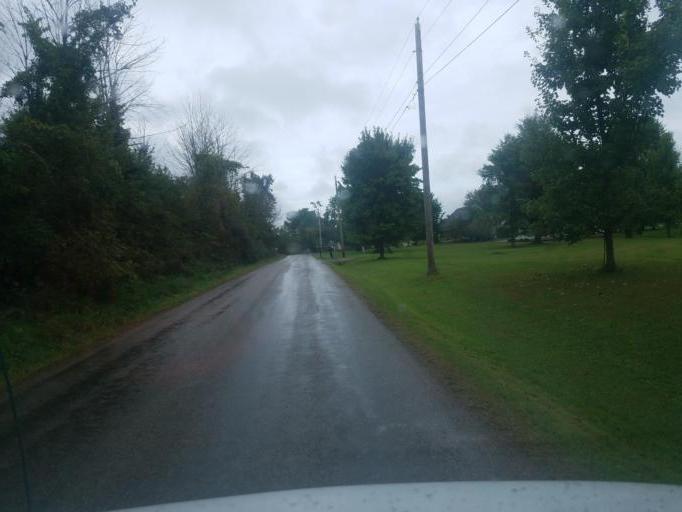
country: US
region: Ohio
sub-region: Wayne County
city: West Salem
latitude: 40.9601
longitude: -82.1159
